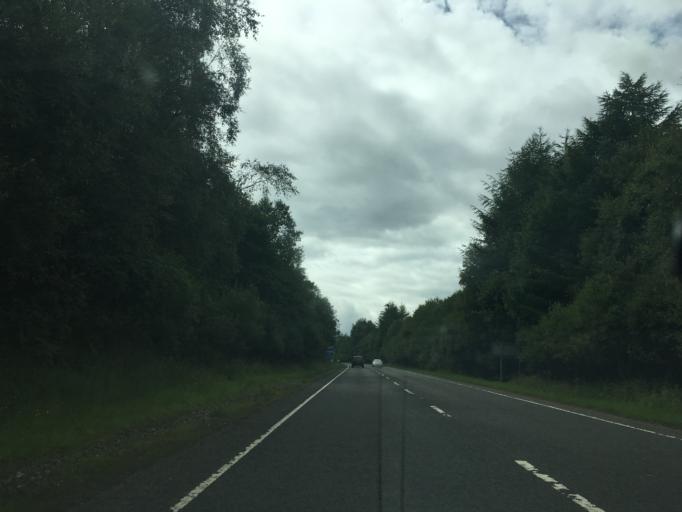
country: GB
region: Scotland
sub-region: Stirling
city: Callander
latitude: 56.3742
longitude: -4.2900
